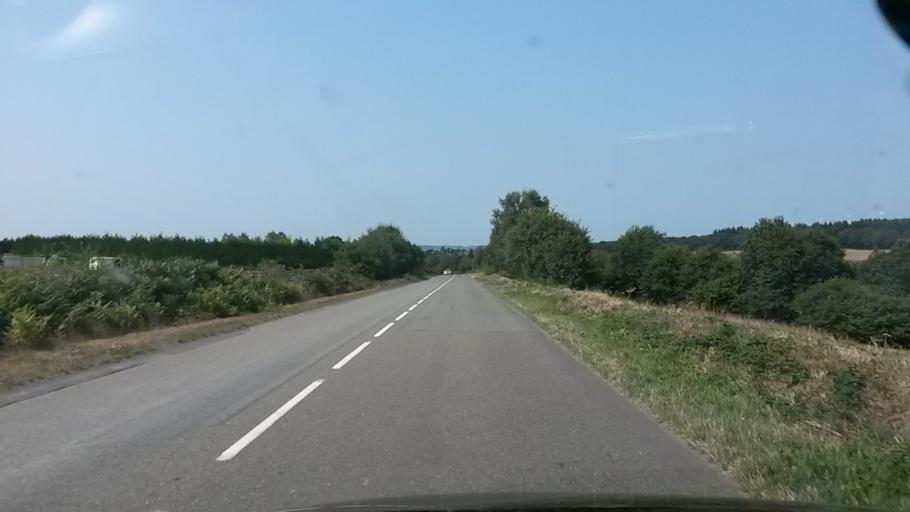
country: FR
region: Pays de la Loire
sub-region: Departement de la Mayenne
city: Villaines-la-Juhel
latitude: 48.3593
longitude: -0.2271
